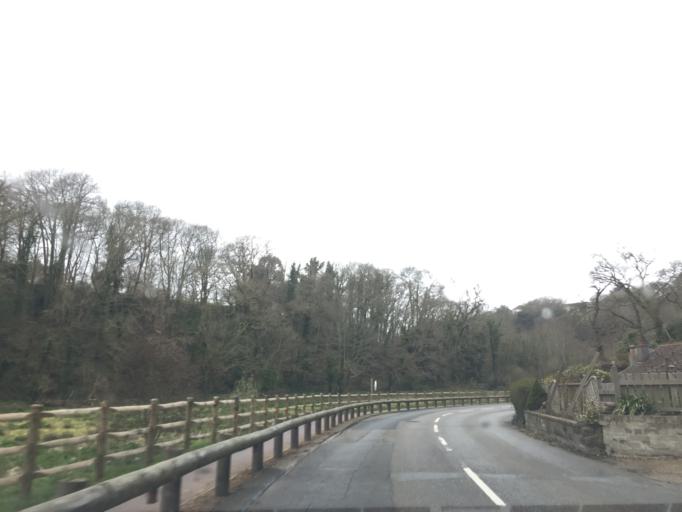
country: JE
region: St Helier
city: Saint Helier
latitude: 49.2064
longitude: -2.1578
